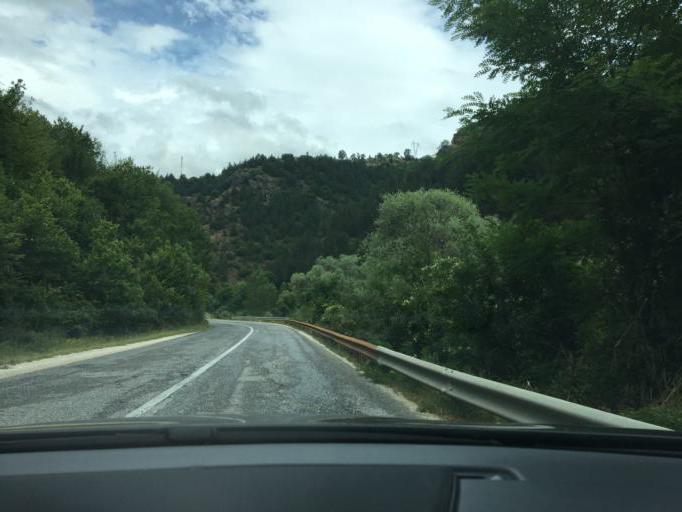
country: MK
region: Kriva Palanka
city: Kriva Palanka
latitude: 42.2293
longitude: 22.3740
